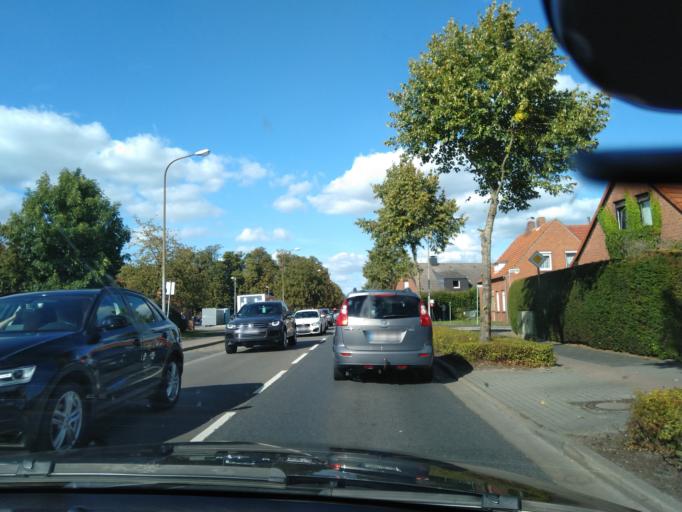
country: DE
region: Lower Saxony
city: Leer
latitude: 53.2448
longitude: 7.4574
